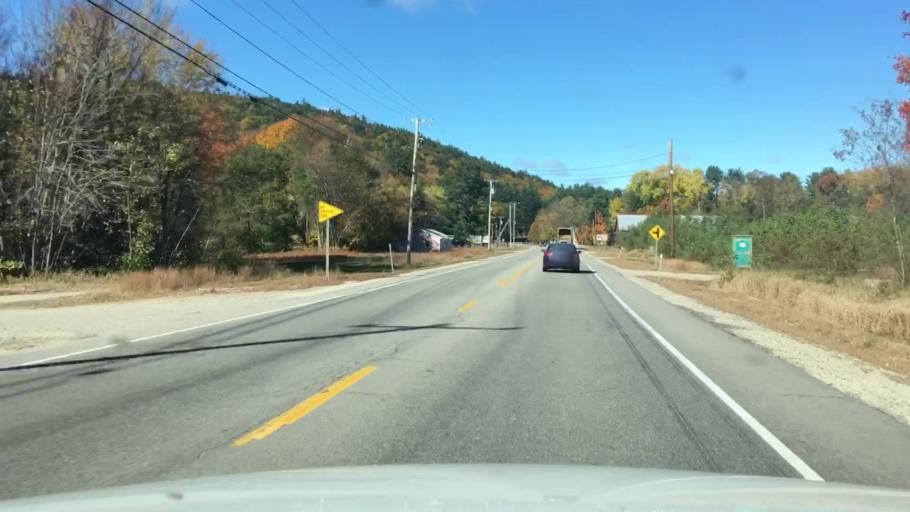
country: US
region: New Hampshire
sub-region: Carroll County
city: Tuftonboro
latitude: 43.7905
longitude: -71.1758
